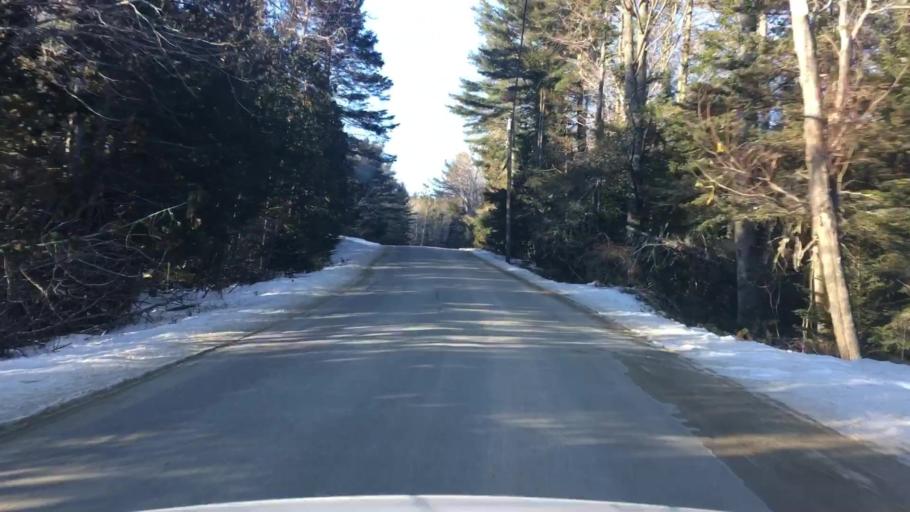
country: US
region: Maine
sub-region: Hancock County
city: Castine
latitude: 44.3395
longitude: -68.7824
